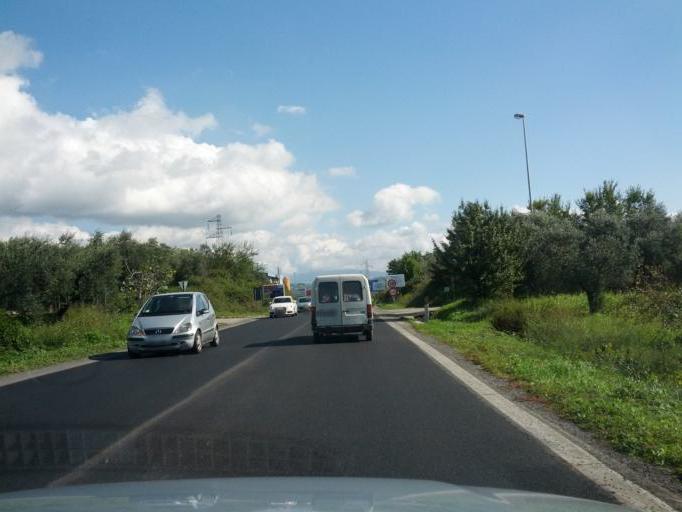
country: IT
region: Latium
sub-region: Provincia di Latina
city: Formia
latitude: 41.2677
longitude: 13.6667
